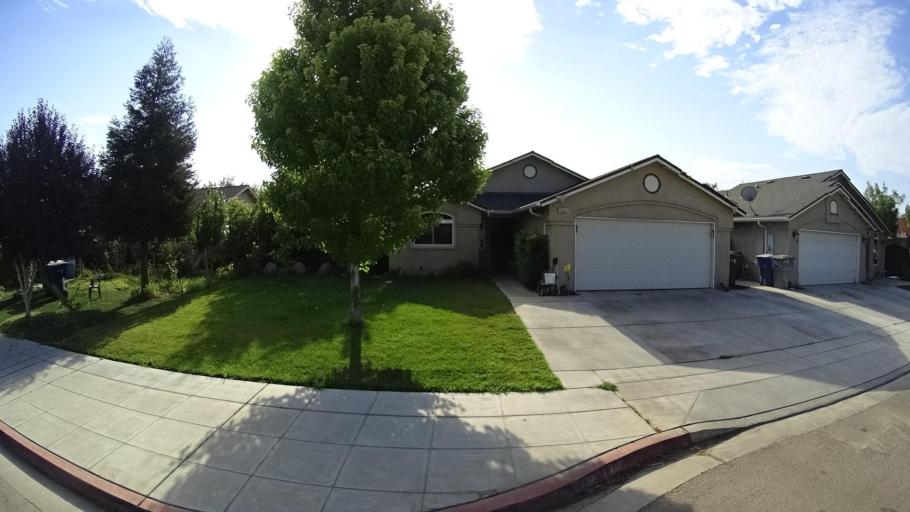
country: US
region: California
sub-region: Fresno County
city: Sunnyside
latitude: 36.7161
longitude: -119.6992
